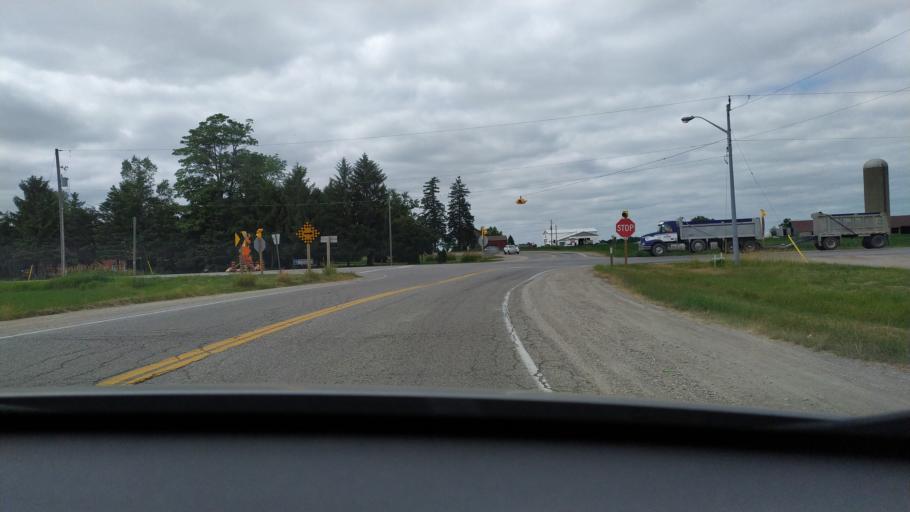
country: CA
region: Ontario
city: Stratford
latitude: 43.3159
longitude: -80.9843
